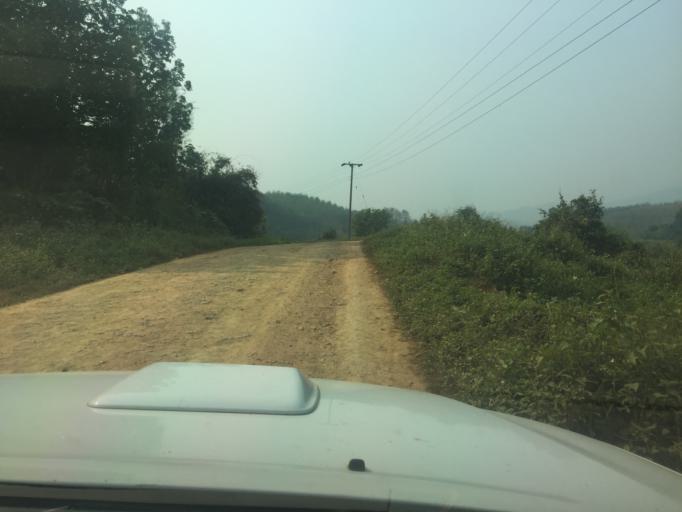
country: TH
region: Phayao
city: Phu Sang
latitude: 19.6679
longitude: 100.5283
